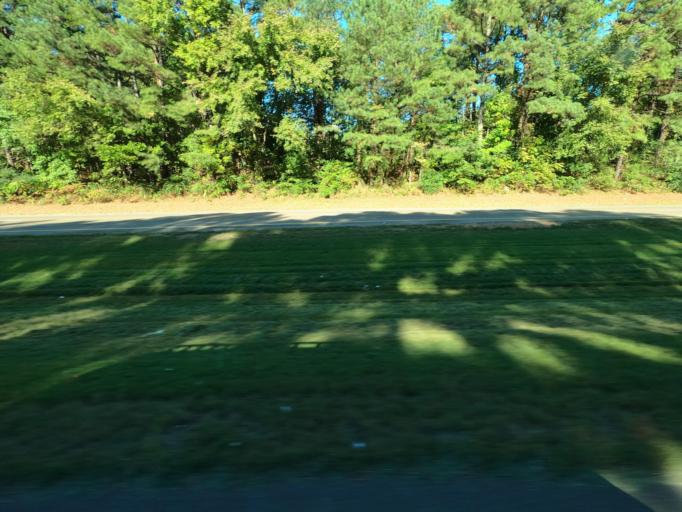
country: US
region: Tennessee
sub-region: Tipton County
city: Brighton
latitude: 35.4846
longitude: -89.7383
